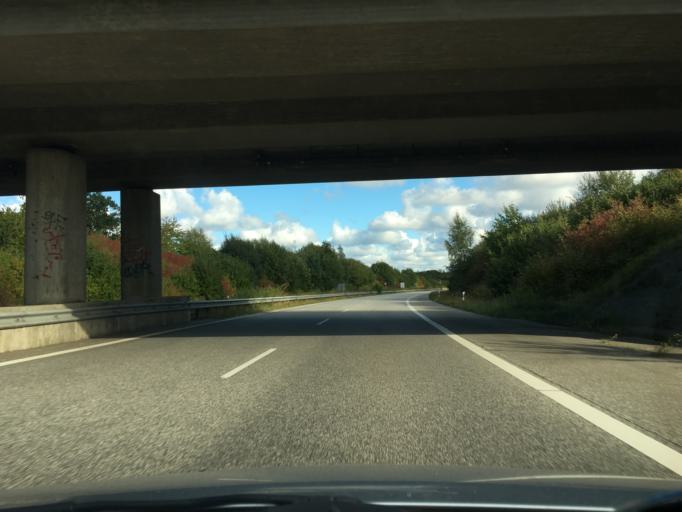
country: DE
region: Schleswig-Holstein
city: Heikendorf
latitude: 54.3592
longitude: 10.2070
